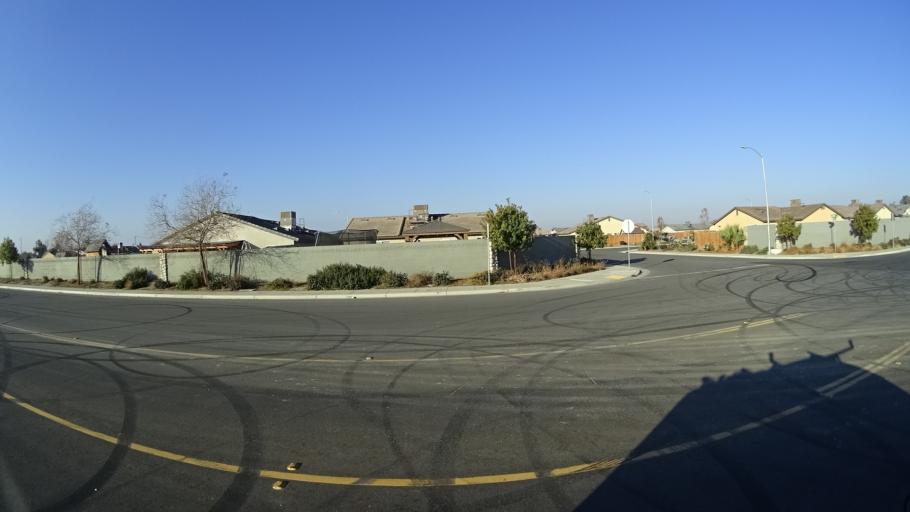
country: US
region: California
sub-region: Kern County
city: Greenfield
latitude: 35.2974
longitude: -118.9942
